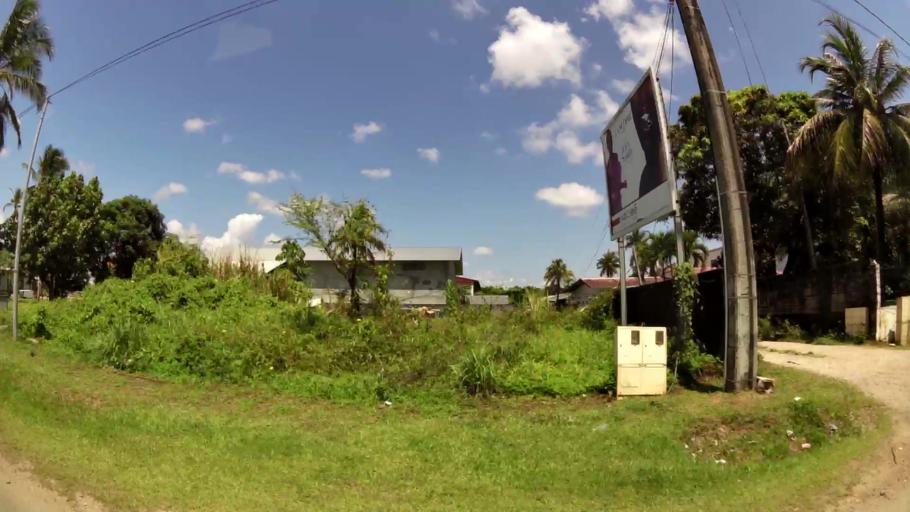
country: GF
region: Guyane
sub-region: Guyane
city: Cayenne
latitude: 4.9022
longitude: -52.3258
